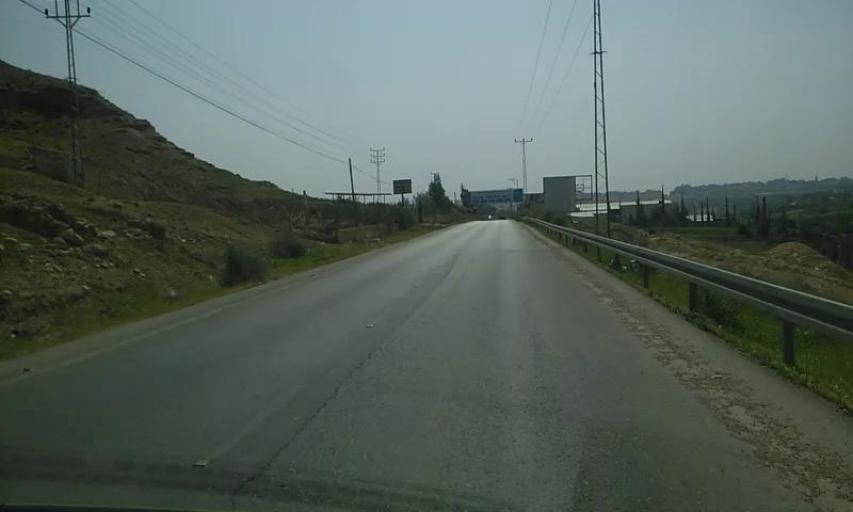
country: PS
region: West Bank
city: An Nuway`imah
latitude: 31.8908
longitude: 35.4313
